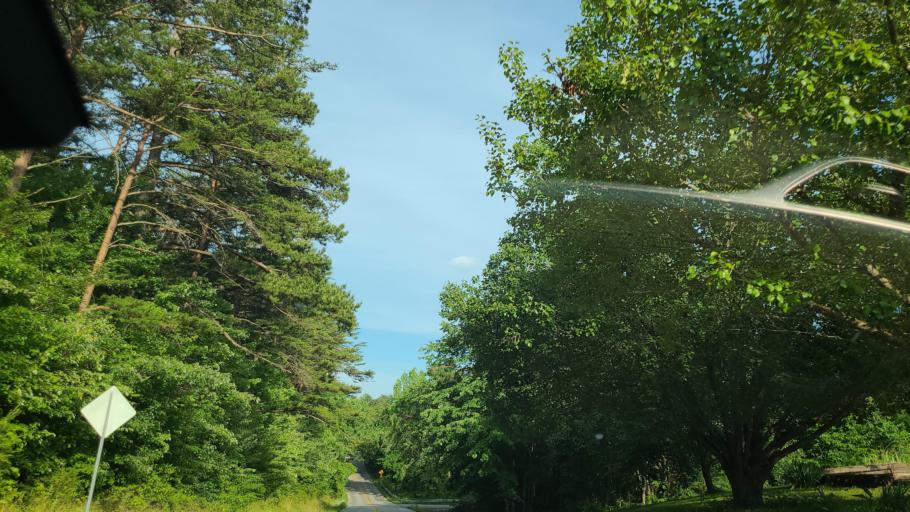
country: US
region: Kentucky
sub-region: Whitley County
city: Corbin
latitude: 36.8833
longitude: -84.2103
